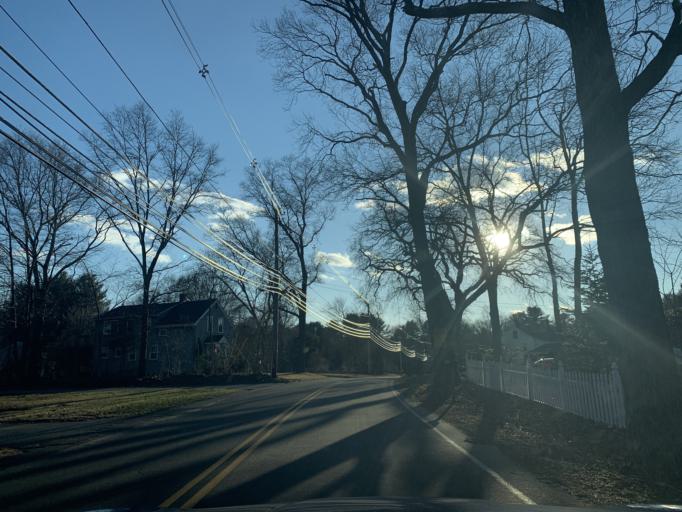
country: US
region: Massachusetts
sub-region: Bristol County
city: Norton
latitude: 41.9538
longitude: -71.1924
